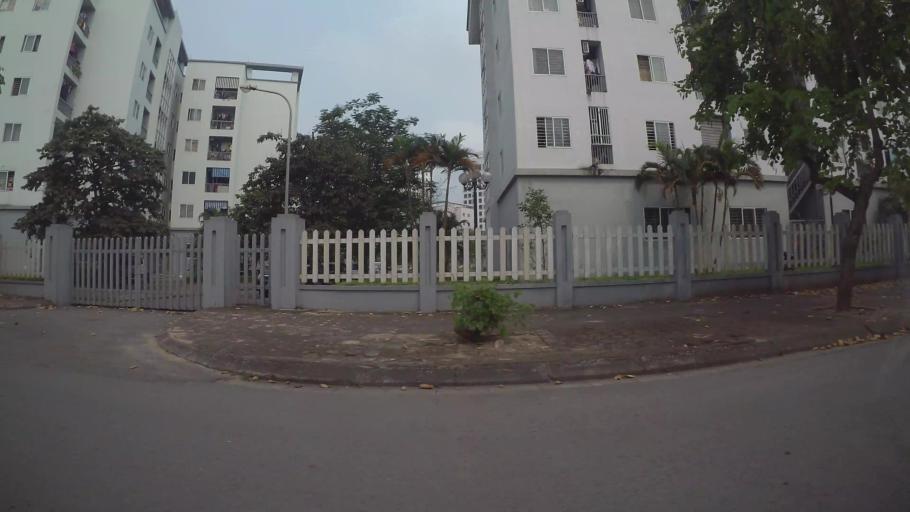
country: VN
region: Ha Noi
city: Trau Quy
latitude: 21.0569
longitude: 105.9105
